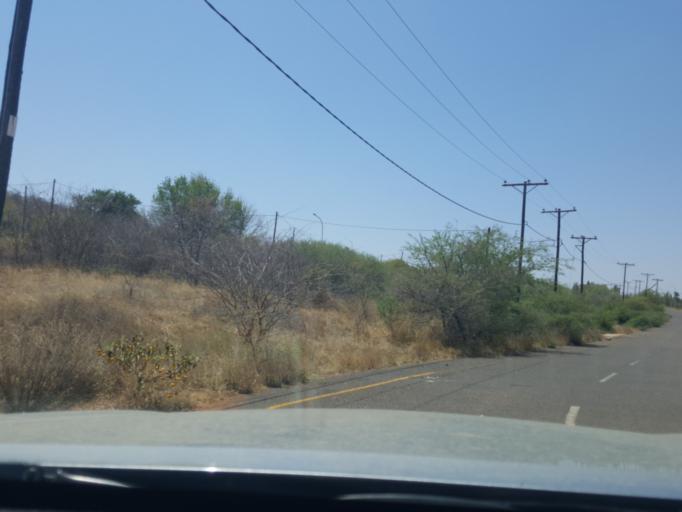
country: BW
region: South East
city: Lobatse
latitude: -25.1840
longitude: 25.6802
